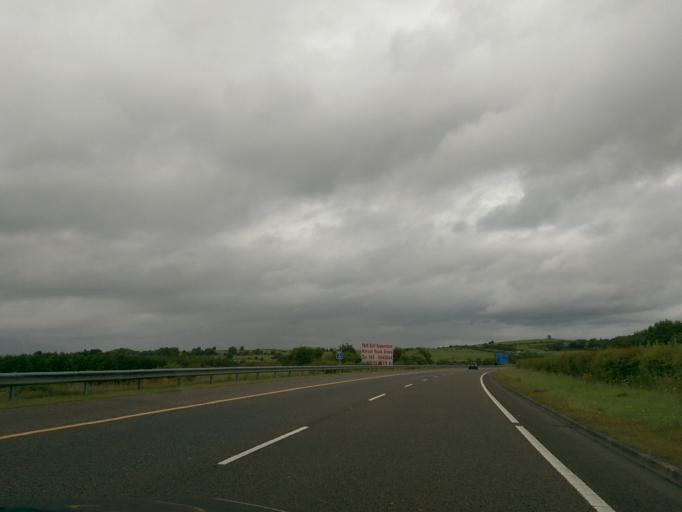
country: IE
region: Munster
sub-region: An Clar
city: Newmarket on Fergus
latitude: 52.7635
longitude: -8.9180
